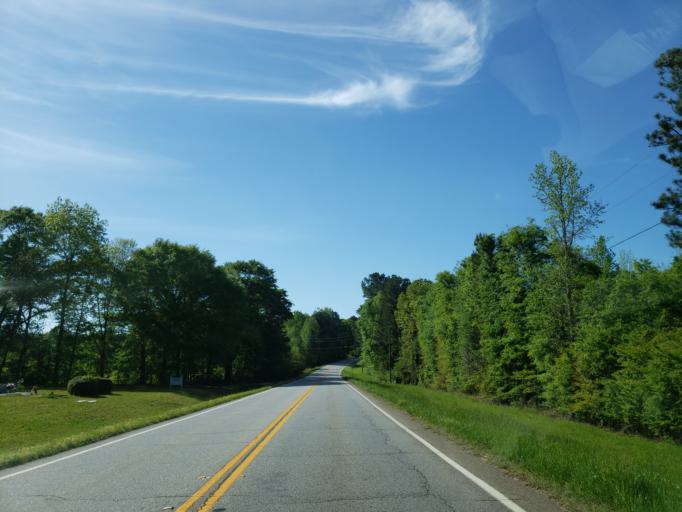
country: US
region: Georgia
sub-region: Haralson County
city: Tallapoosa
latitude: 33.6999
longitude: -85.2677
